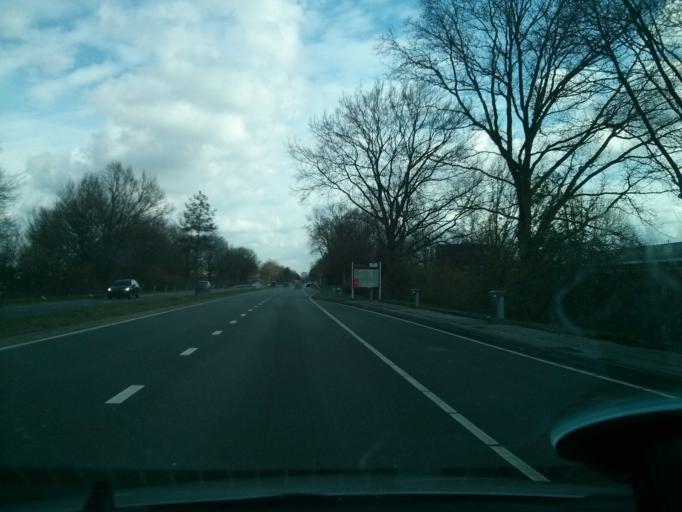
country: NL
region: North Brabant
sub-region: Gemeente Eindhoven
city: Meerhoven
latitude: 51.4468
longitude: 5.4361
